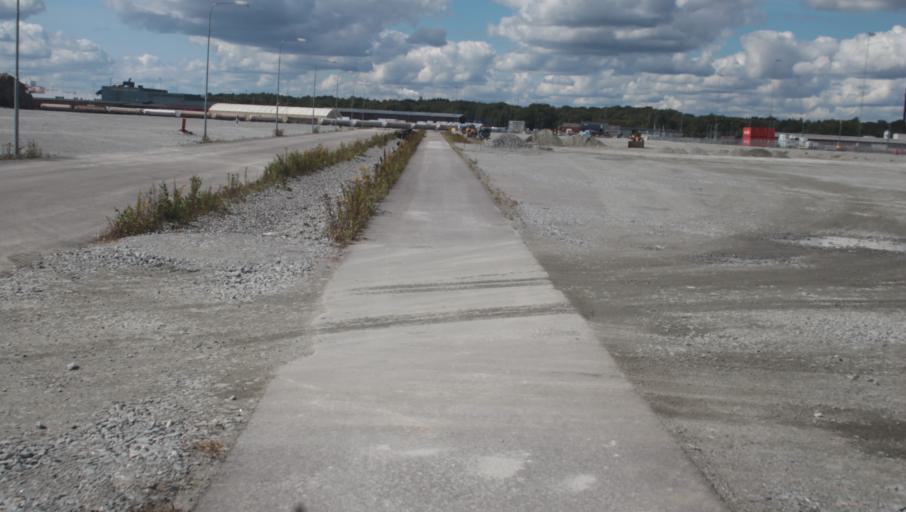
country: SE
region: Blekinge
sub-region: Karlshamns Kommun
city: Karlshamn
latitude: 56.1625
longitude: 14.8346
